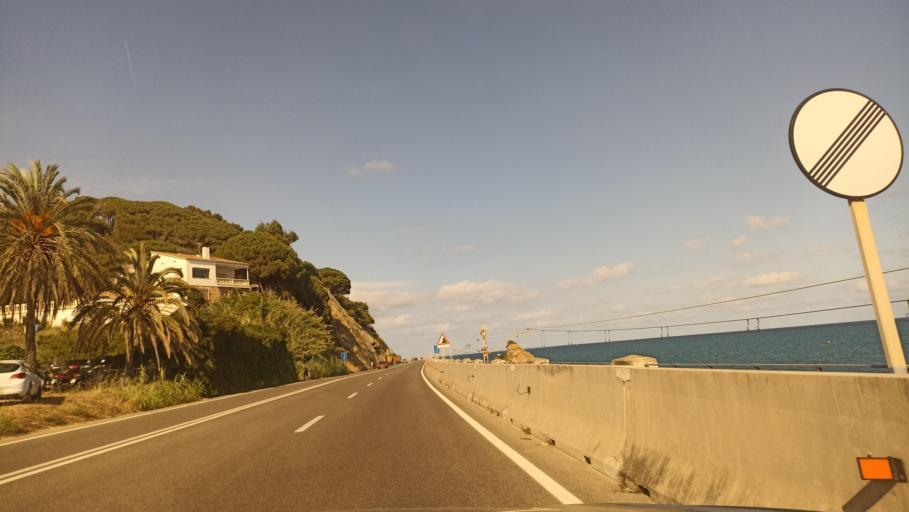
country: ES
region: Catalonia
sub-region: Provincia de Barcelona
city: Sant Pol de Mar
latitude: 41.5943
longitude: 2.6036
